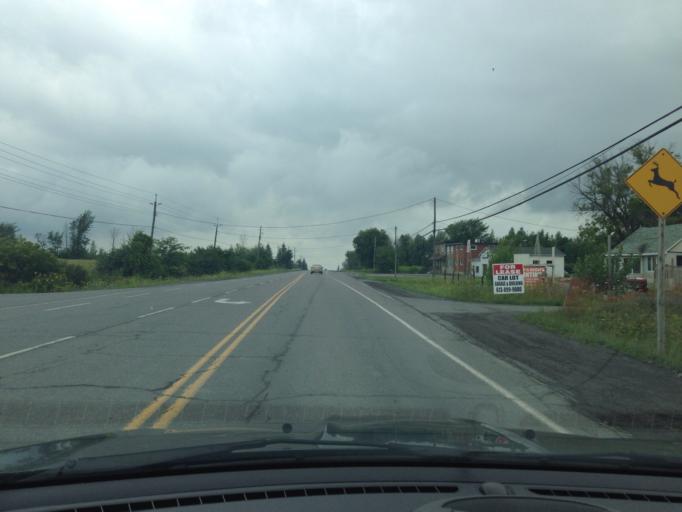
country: CA
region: Ontario
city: Ottawa
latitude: 45.2975
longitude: -75.5803
